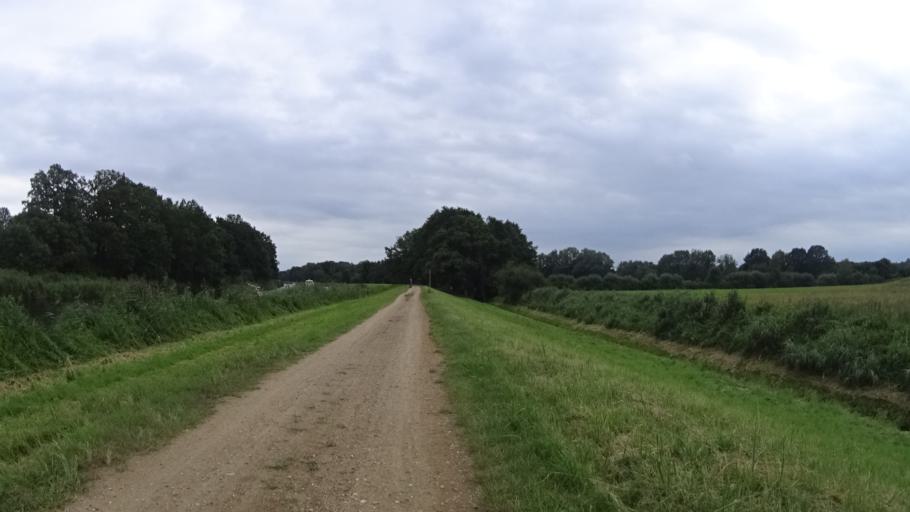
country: DE
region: Schleswig-Holstein
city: Panten
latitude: 53.6620
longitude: 10.6385
